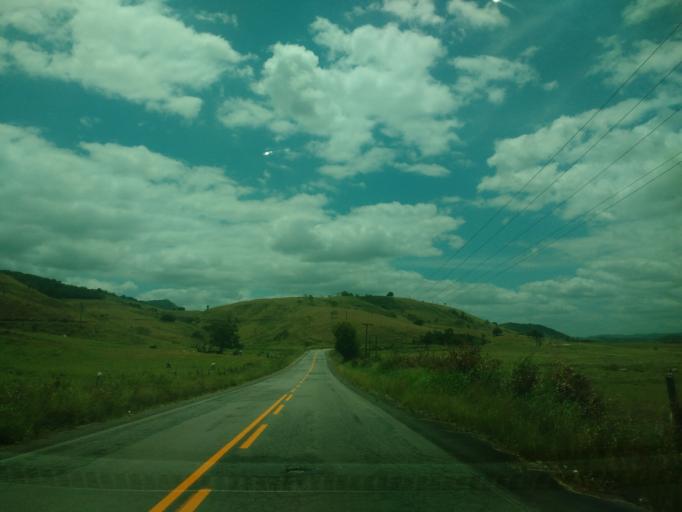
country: BR
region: Alagoas
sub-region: Uniao Dos Palmares
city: Uniao dos Palmares
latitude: -9.1435
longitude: -36.0591
